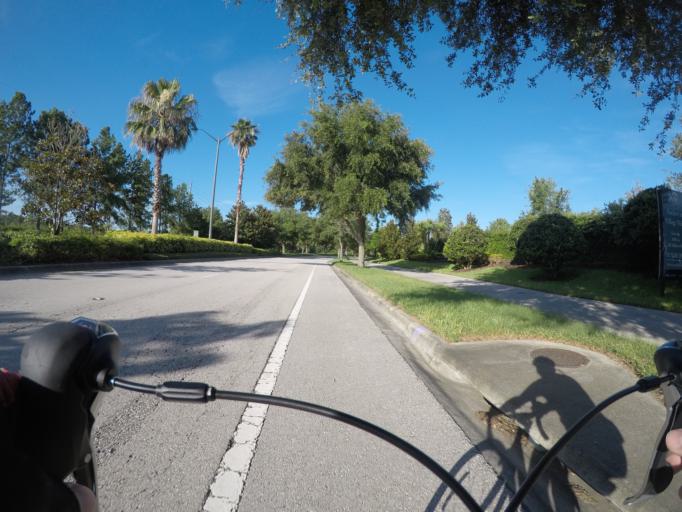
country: US
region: Florida
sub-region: Orange County
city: Meadow Woods
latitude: 28.3968
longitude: -81.2521
